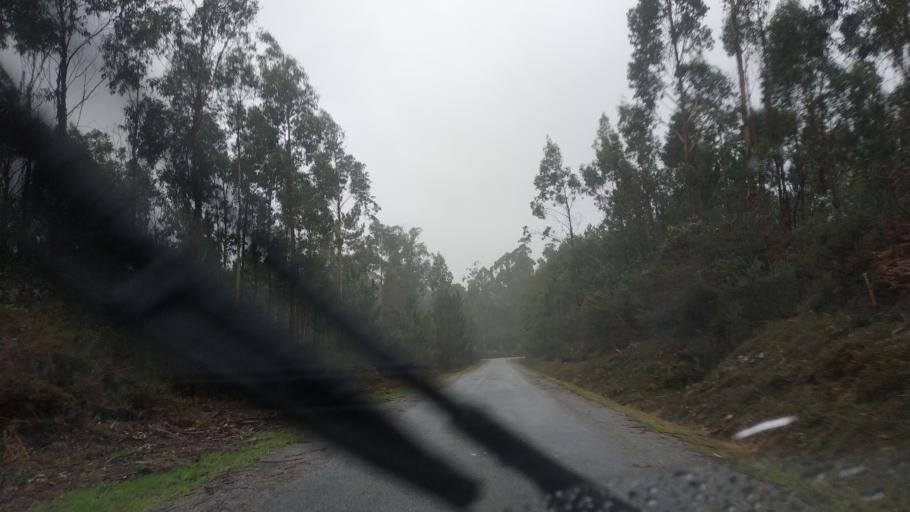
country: ES
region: Galicia
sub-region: Provincia da Coruna
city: Negreira
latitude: 42.9093
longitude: -8.7675
